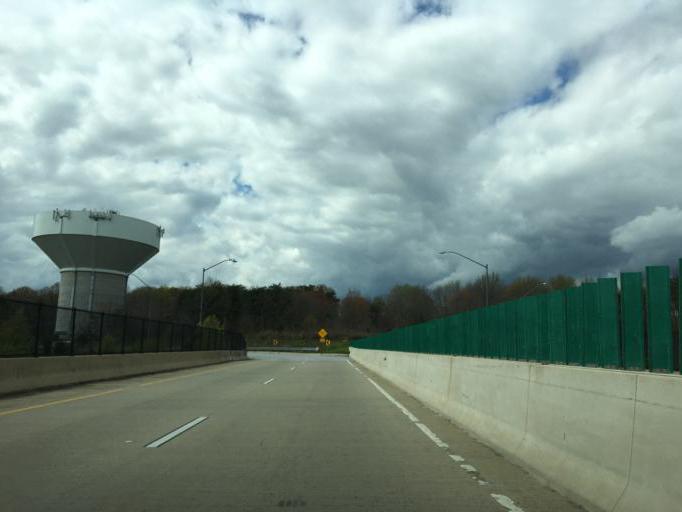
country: US
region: Maryland
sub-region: Anne Arundel County
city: Jessup
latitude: 39.1562
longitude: -76.7453
